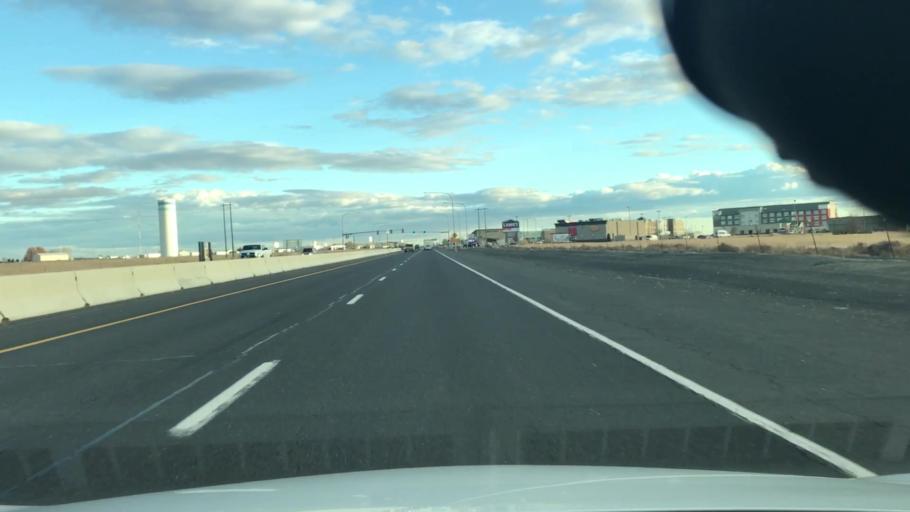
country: US
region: Washington
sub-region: Grant County
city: Moses Lake
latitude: 47.1082
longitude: -119.2544
